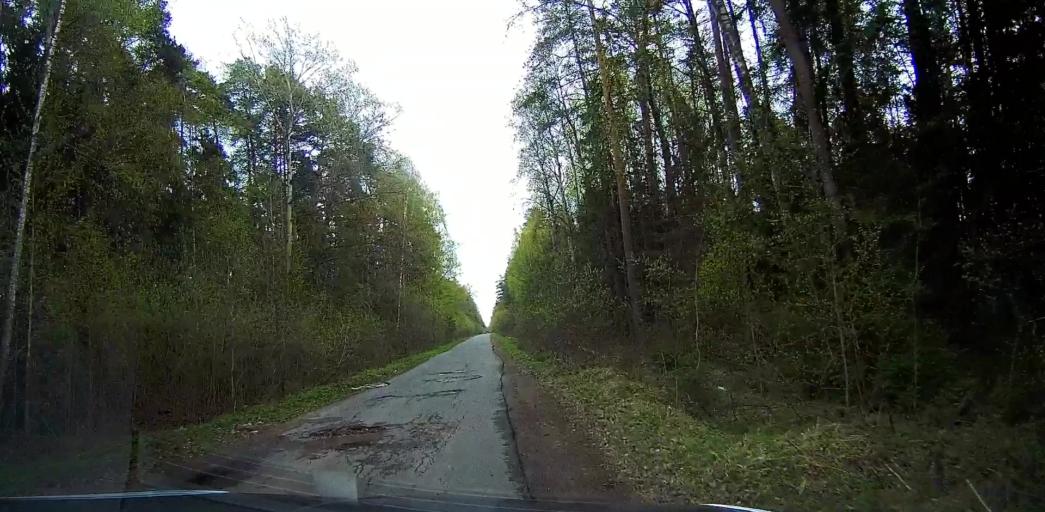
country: RU
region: Moskovskaya
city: Malyshevo
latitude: 55.5505
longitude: 38.3541
